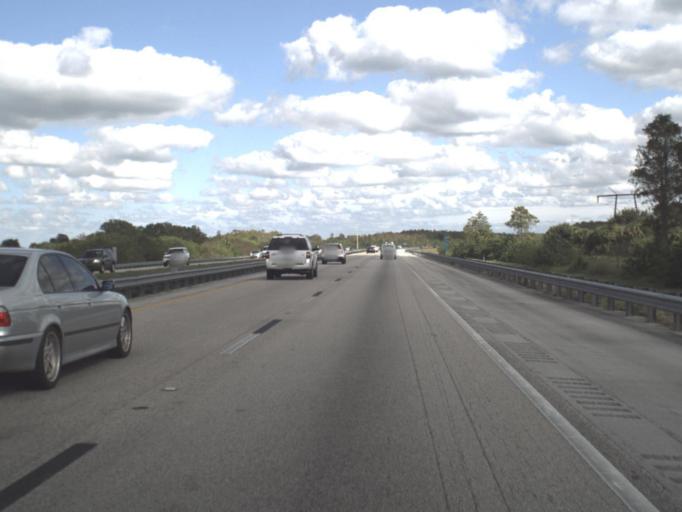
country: US
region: Florida
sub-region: Indian River County
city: West Vero Corridor
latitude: 27.5593
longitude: -80.6554
